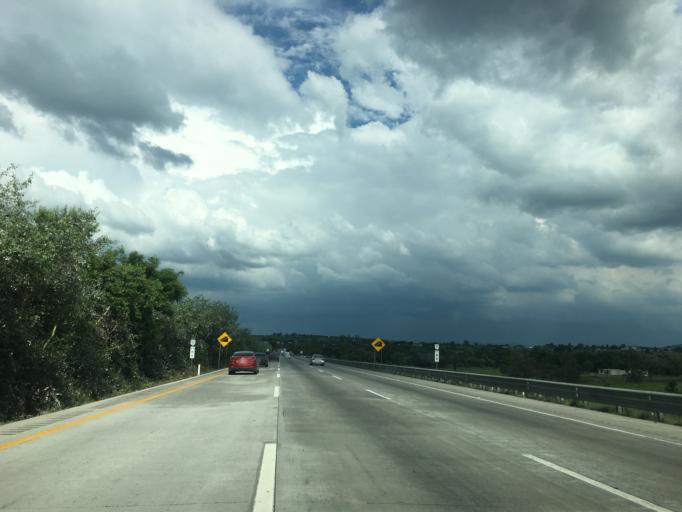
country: MX
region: Mexico
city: San Francisco Soyaniquilpan
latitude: 19.9882
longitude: -99.4540
